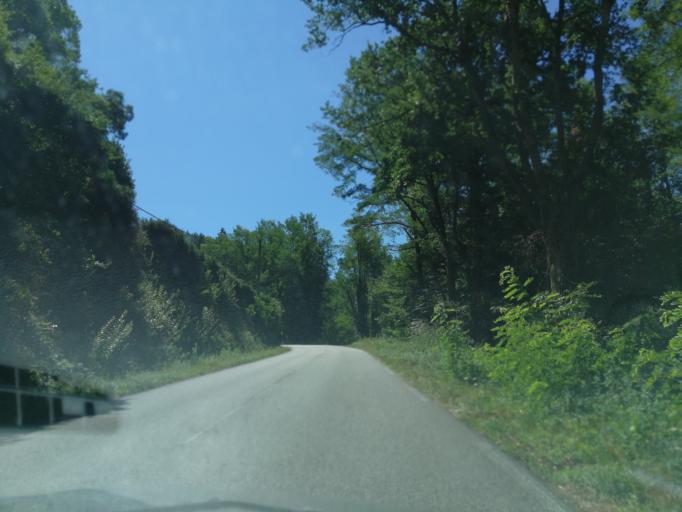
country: FR
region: Limousin
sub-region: Departement de la Correze
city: Argentat
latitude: 45.0763
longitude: 1.9446
